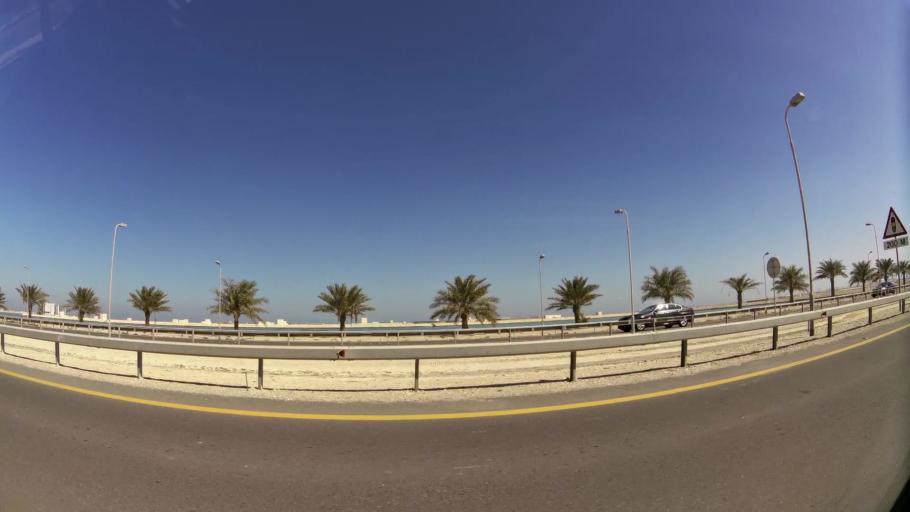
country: BH
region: Muharraq
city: Al Hadd
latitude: 26.2574
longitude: 50.6602
